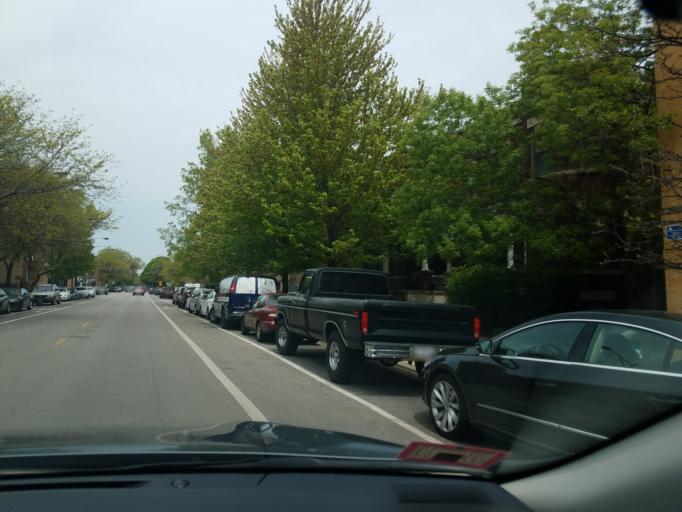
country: US
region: Illinois
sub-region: Cook County
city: Lincolnwood
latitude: 41.9530
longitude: -87.6642
